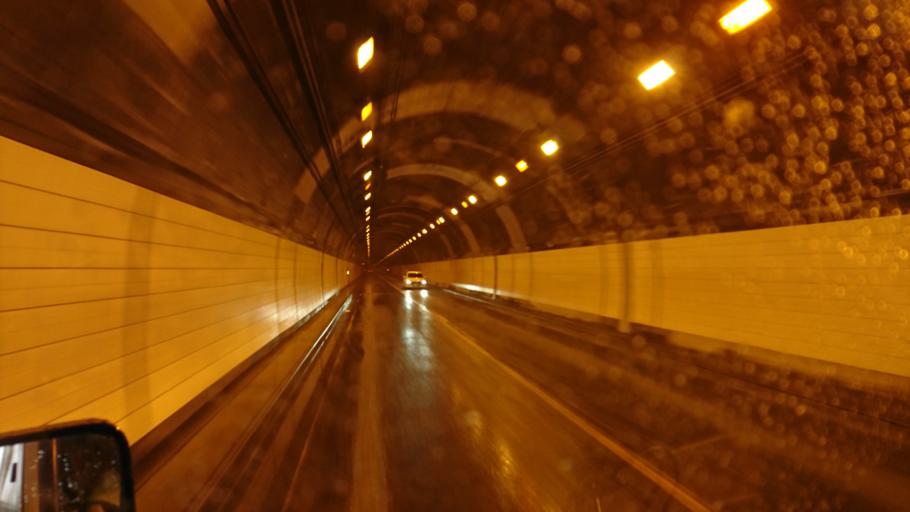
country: JP
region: Hyogo
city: Toyooka
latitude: 35.5015
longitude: 134.5368
